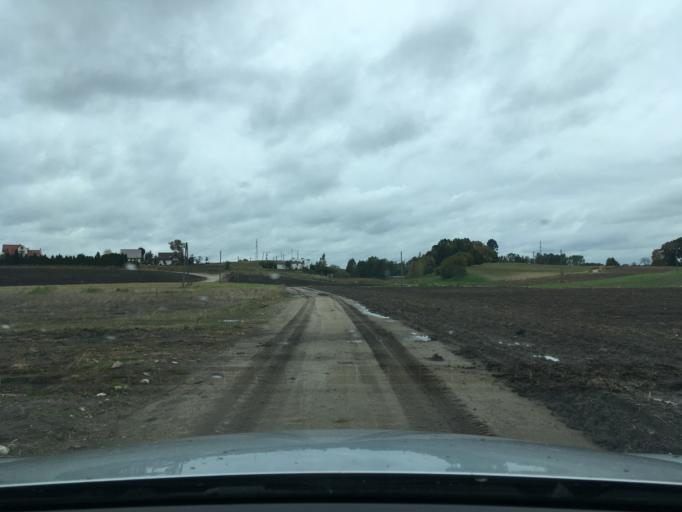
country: PL
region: Pomeranian Voivodeship
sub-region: Powiat koscierski
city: Koscierzyna
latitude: 54.1039
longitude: 17.9807
